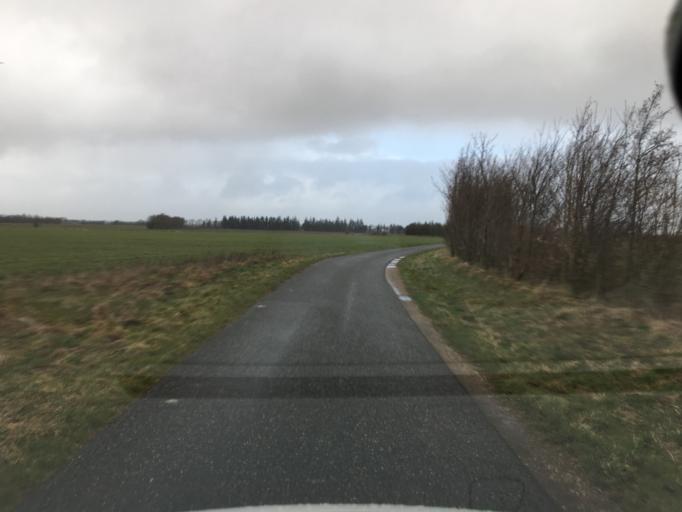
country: DK
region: South Denmark
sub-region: Aabenraa Kommune
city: Tinglev
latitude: 54.9495
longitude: 9.1604
